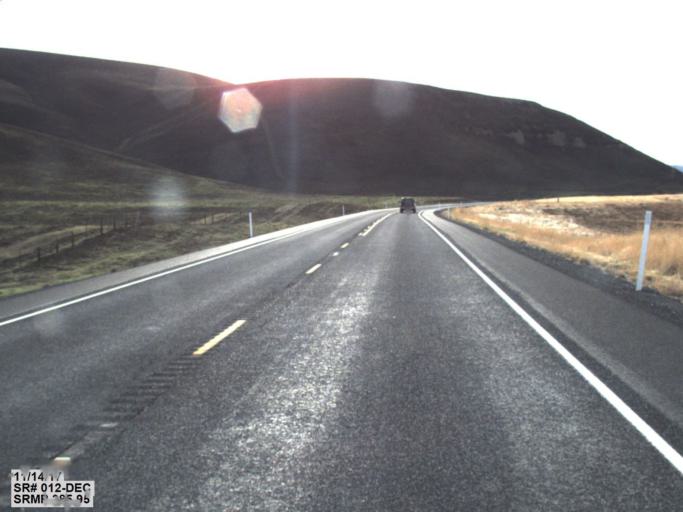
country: US
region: Washington
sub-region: Columbia County
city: Dayton
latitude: 46.5341
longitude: -117.9081
